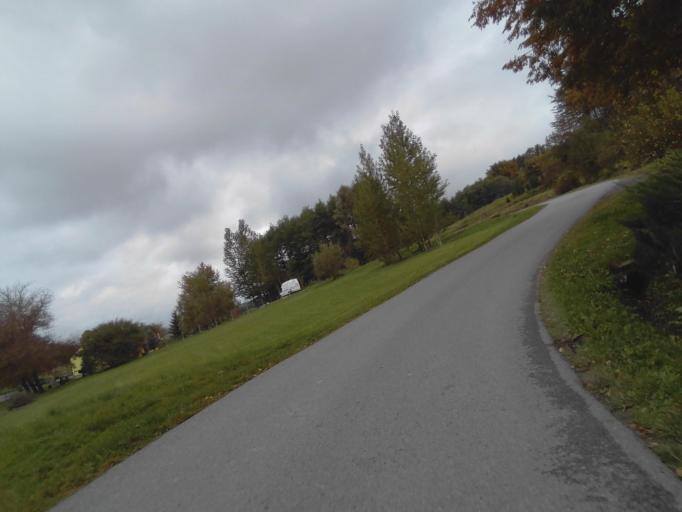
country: PL
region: Subcarpathian Voivodeship
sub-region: Powiat strzyzowski
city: Gwoznica Gorna
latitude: 49.8342
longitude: 22.0003
